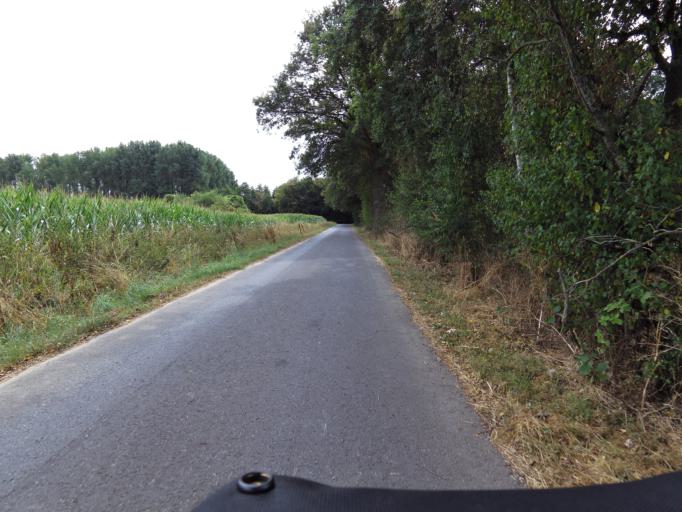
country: DE
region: North Rhine-Westphalia
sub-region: Regierungsbezirk Dusseldorf
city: Kevelaer
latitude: 51.5860
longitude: 6.2085
